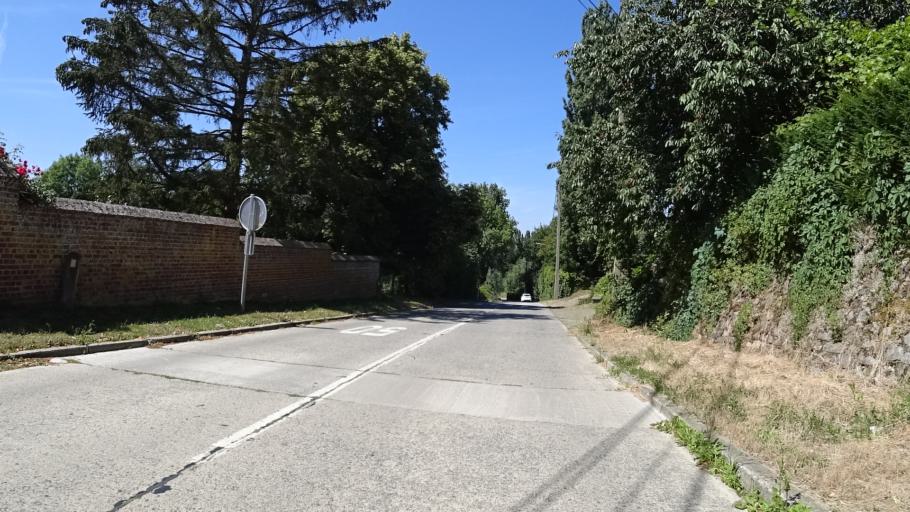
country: BE
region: Wallonia
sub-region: Province du Brabant Wallon
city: Jodoigne
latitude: 50.6865
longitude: 4.8436
